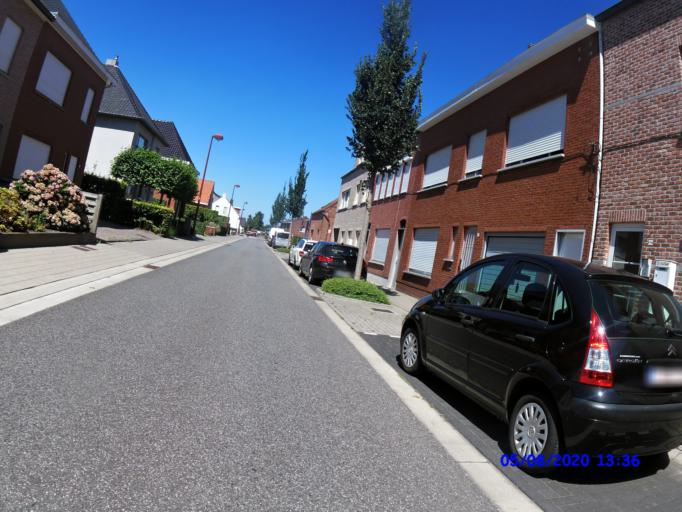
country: BE
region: Flanders
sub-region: Provincie Antwerpen
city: Rijkevorsel
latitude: 51.3521
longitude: 4.7577
